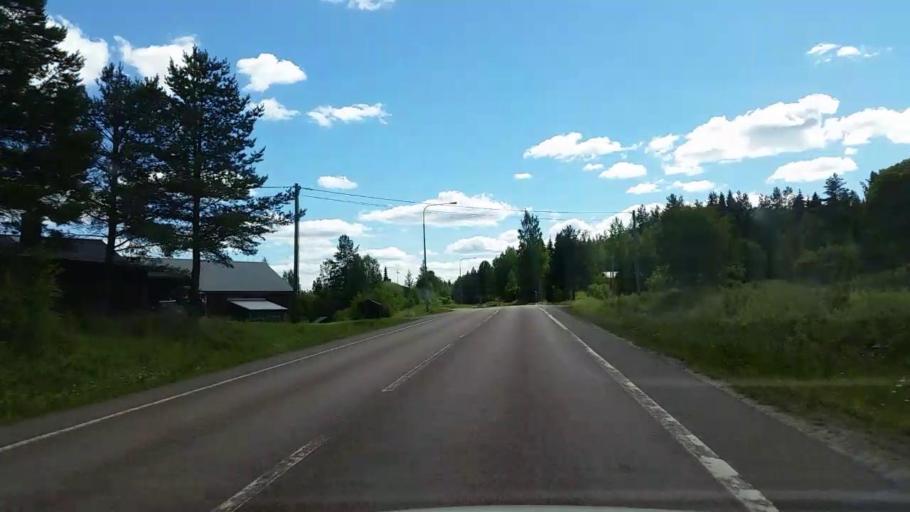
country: SE
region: Dalarna
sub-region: Faluns Kommun
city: Svardsjo
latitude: 60.8393
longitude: 15.7611
